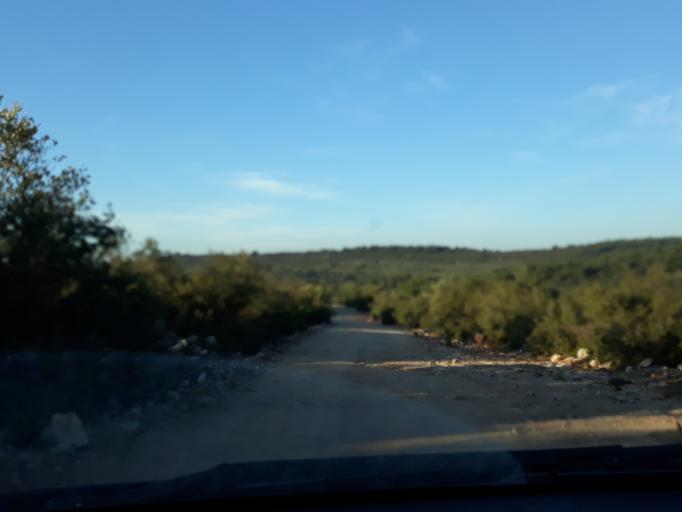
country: GR
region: Central Greece
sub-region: Nomos Voiotias
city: Asopia
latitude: 38.2597
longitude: 23.5352
